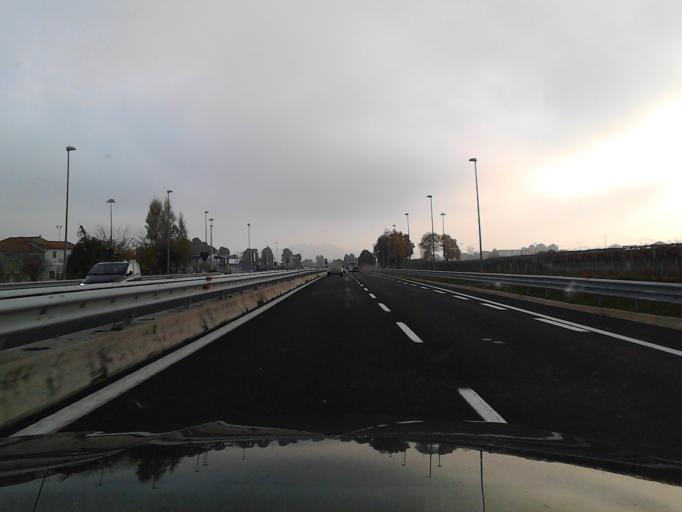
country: IT
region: Abruzzo
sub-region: Provincia di Chieti
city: Francavilla al Mare
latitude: 42.3901
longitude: 14.2886
